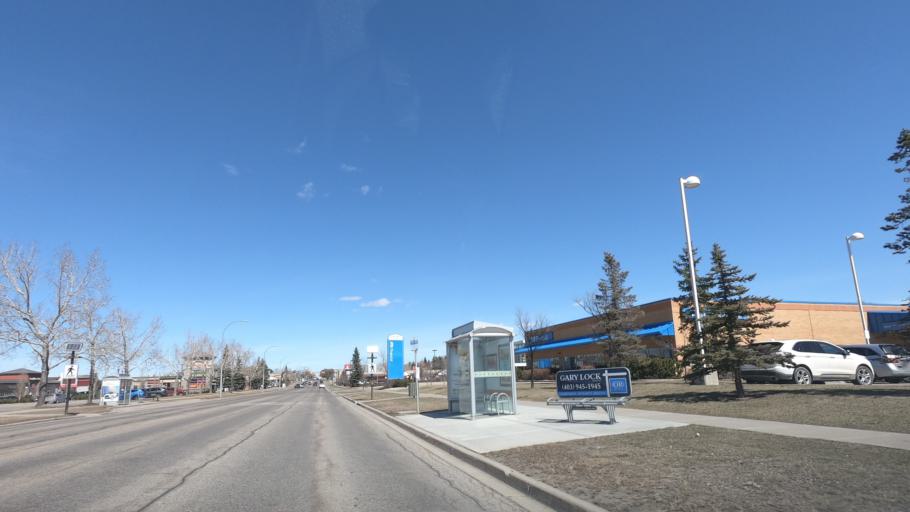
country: CA
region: Alberta
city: Airdrie
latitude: 51.2873
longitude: -114.0133
